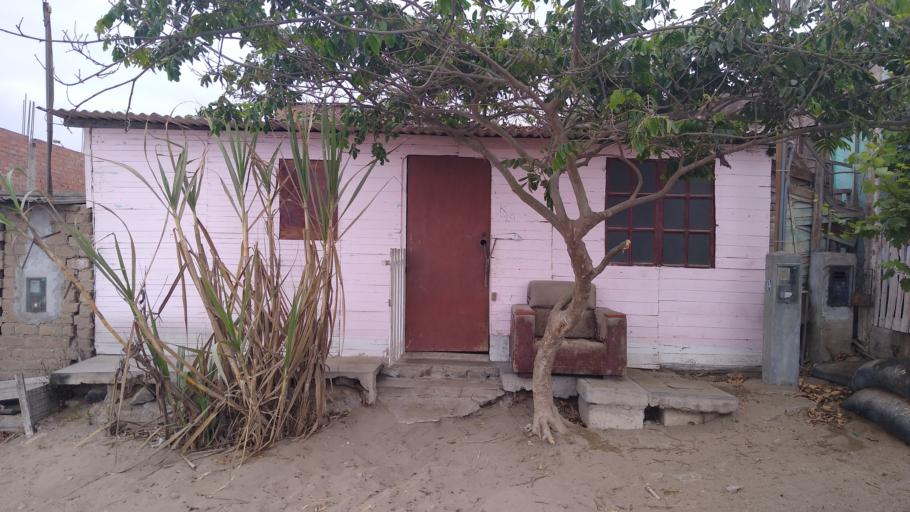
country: PE
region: Lima
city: Ventanilla
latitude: -11.8526
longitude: -77.1498
